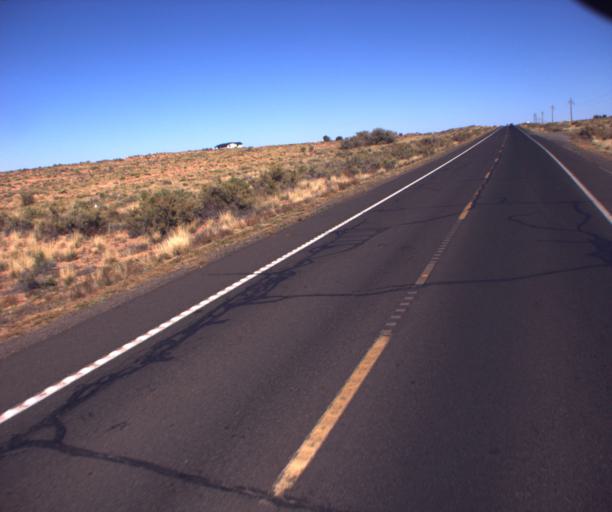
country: US
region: Arizona
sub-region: Coconino County
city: Tuba City
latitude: 36.1260
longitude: -111.1996
